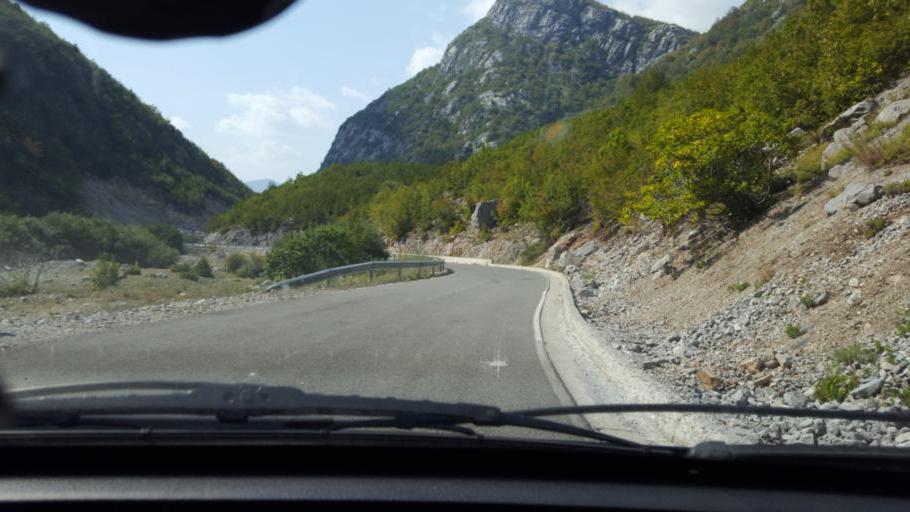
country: AL
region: Shkoder
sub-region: Rrethi i Malesia e Madhe
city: Kastrat
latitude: 42.5323
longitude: 19.6495
